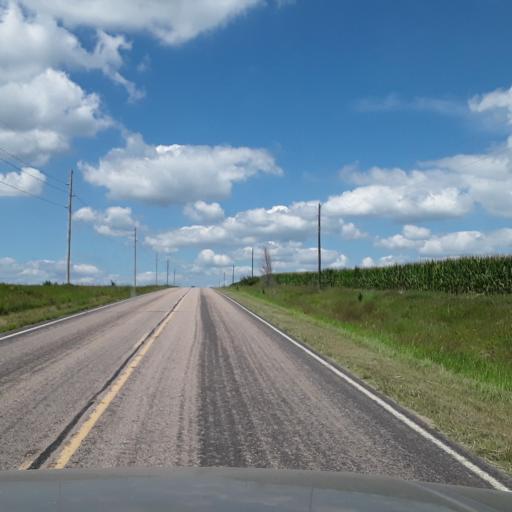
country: US
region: Nebraska
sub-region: Nance County
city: Genoa
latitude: 41.5172
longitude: -97.6960
